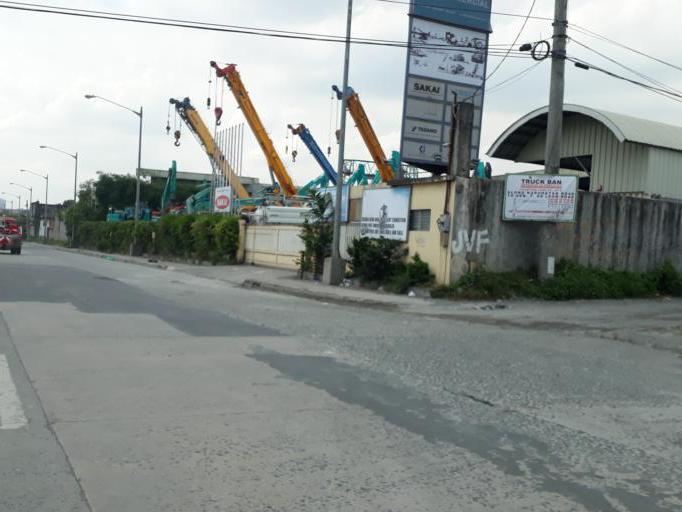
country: PH
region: Calabarzon
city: Bagong Pagasa
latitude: 14.6969
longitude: 121.0188
